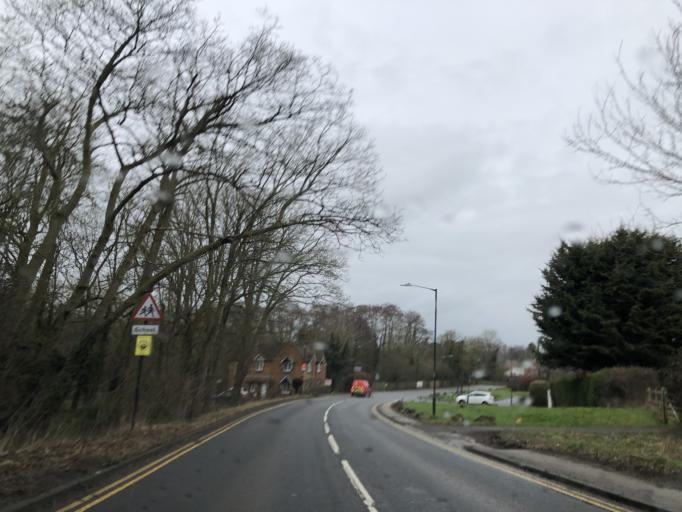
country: GB
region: England
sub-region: Warwickshire
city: Henley in Arden
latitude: 52.2866
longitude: -1.7741
